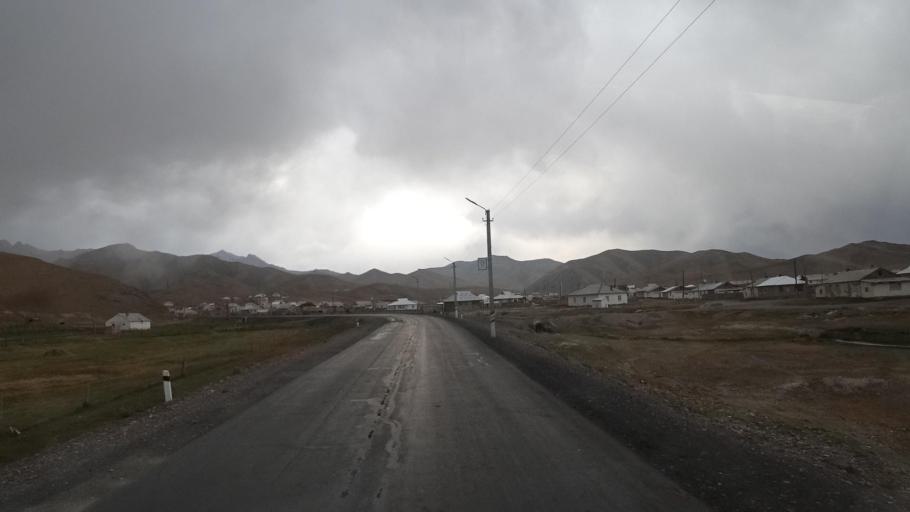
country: KG
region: Osh
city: Gul'cha
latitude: 39.7222
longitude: 73.2474
